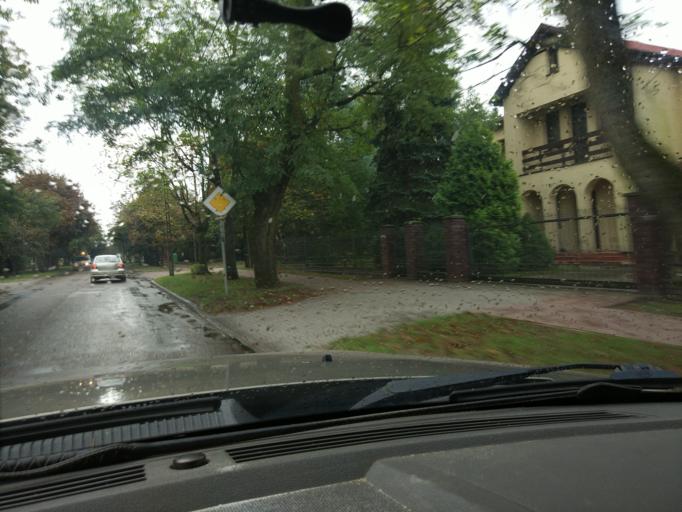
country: PL
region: Masovian Voivodeship
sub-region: Powiat grodziski
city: Podkowa Lesna
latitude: 52.1260
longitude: 20.7212
